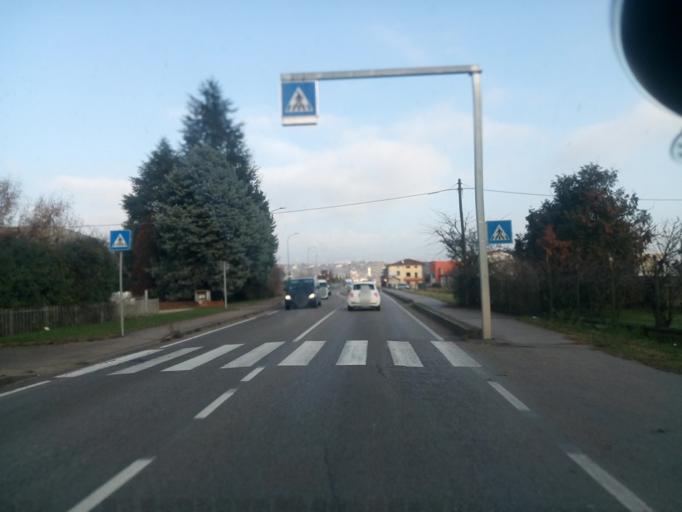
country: IT
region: Veneto
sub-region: Provincia di Vicenza
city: Breganze
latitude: 45.6897
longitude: 11.5626
